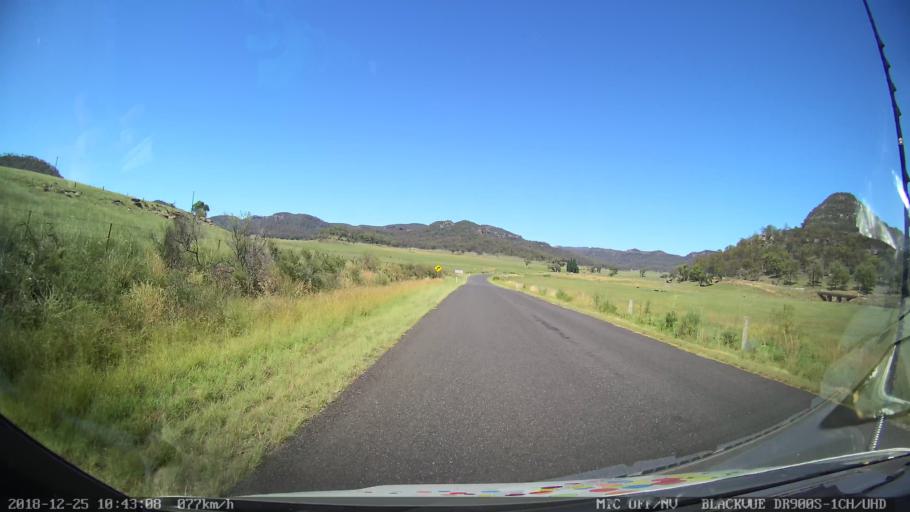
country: AU
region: New South Wales
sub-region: Upper Hunter Shire
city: Merriwa
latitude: -32.4204
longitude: 150.3163
